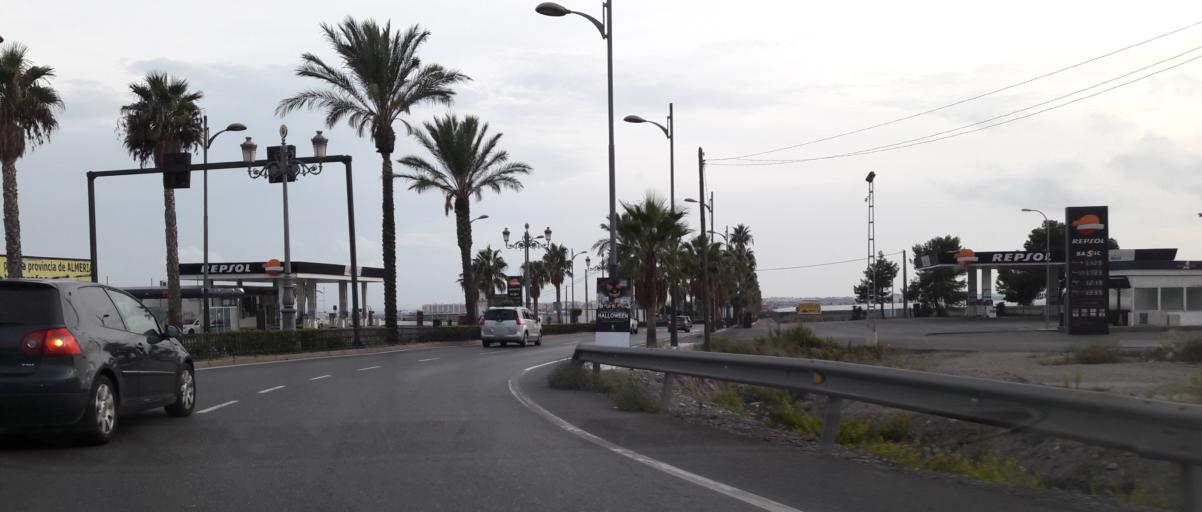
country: ES
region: Andalusia
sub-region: Provincia de Almeria
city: Aguadulce
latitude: 36.7996
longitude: -2.6015
